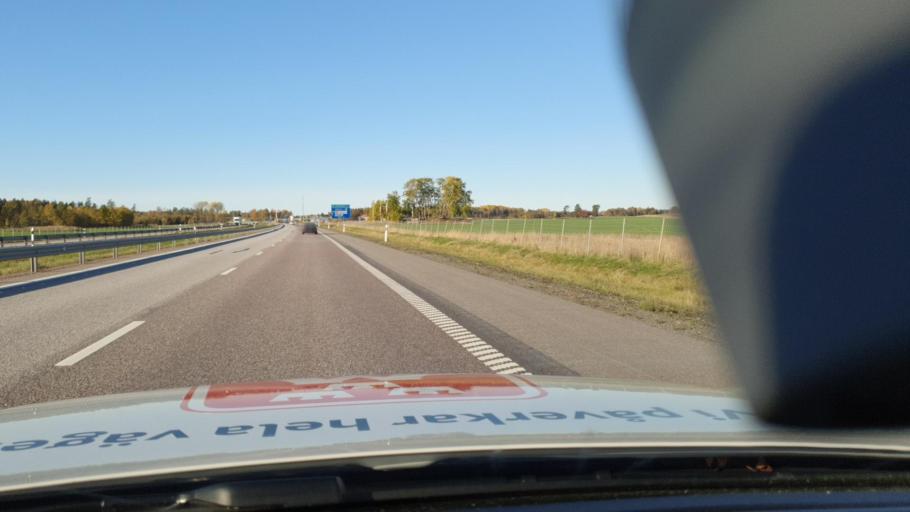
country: SE
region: Vaestmanland
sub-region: Arboga Kommun
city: Arboga
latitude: 59.4267
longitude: 15.8491
